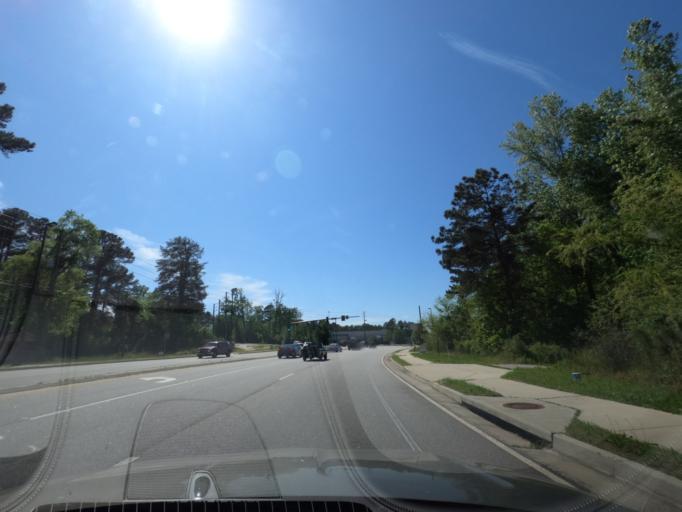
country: US
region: Georgia
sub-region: Columbia County
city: Martinez
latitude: 33.4646
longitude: -82.0909
